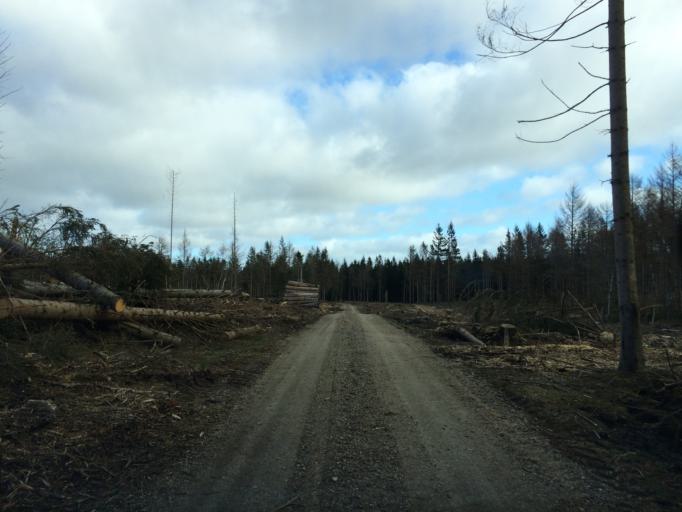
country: DK
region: Central Jutland
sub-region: Holstebro Kommune
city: Ulfborg
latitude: 56.2702
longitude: 8.4465
